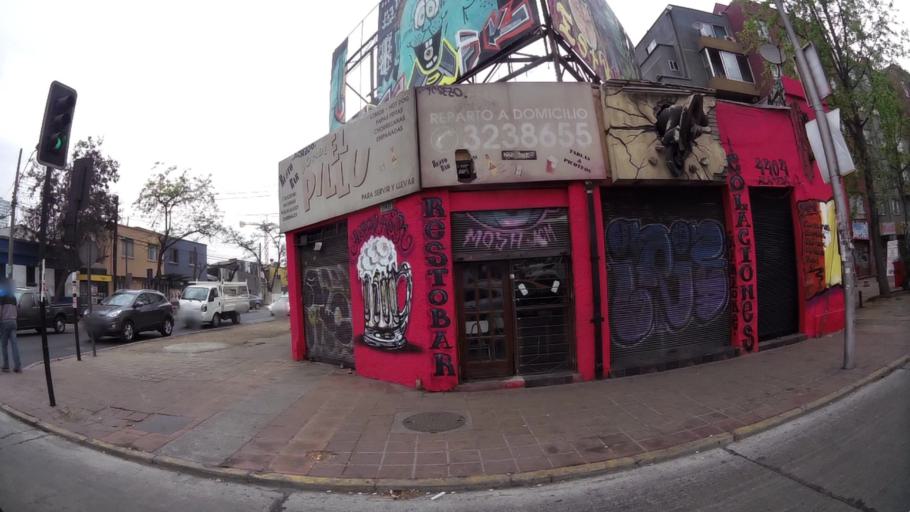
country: CL
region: Santiago Metropolitan
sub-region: Provincia de Santiago
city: Lo Prado
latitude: -33.4553
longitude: -70.6959
